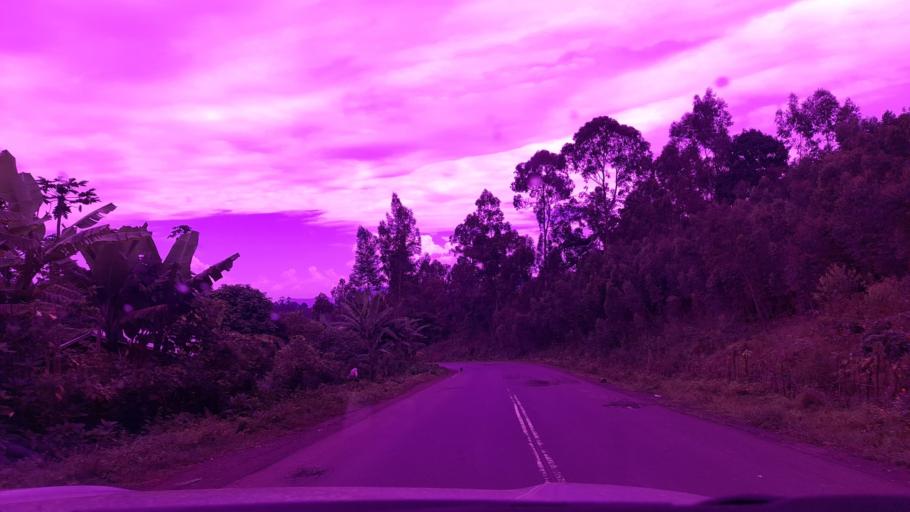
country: ET
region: Southern Nations, Nationalities, and People's Region
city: Mizan Teferi
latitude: 7.0631
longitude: 35.6292
